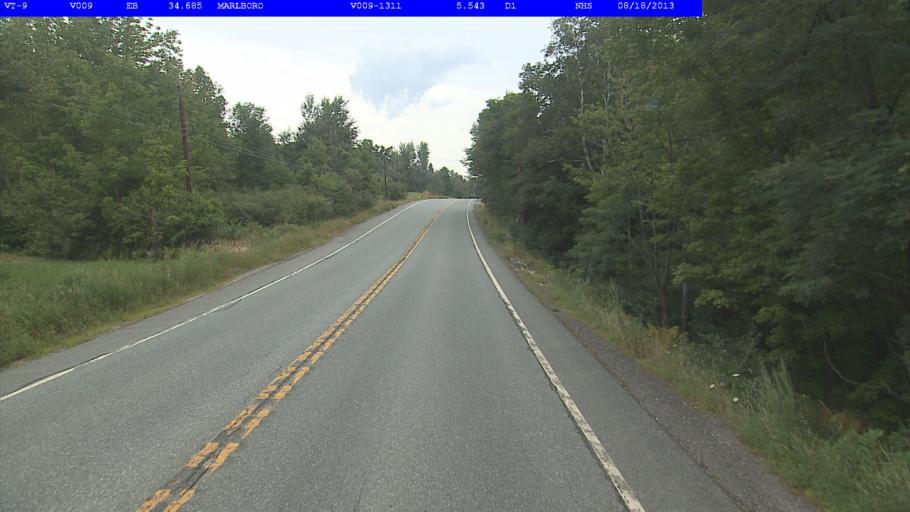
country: US
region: Vermont
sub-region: Windham County
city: Dover
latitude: 42.8678
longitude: -72.7210
